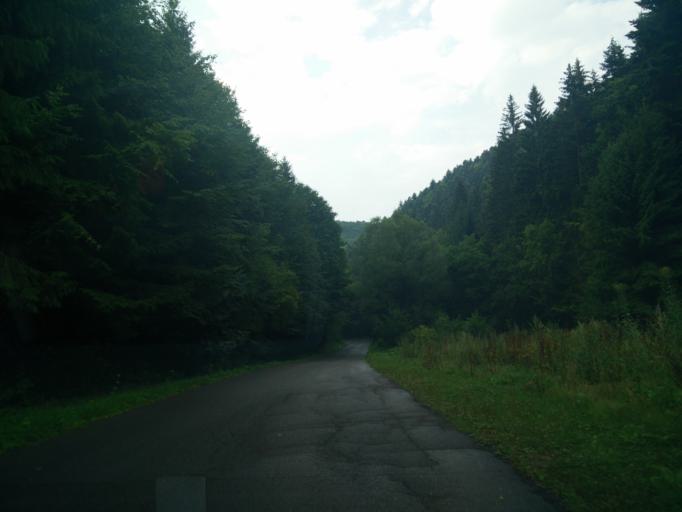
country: SK
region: Banskobystricky
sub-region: Okres Banska Bystrica
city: Banska Stiavnica
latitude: 48.4907
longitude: 18.8464
